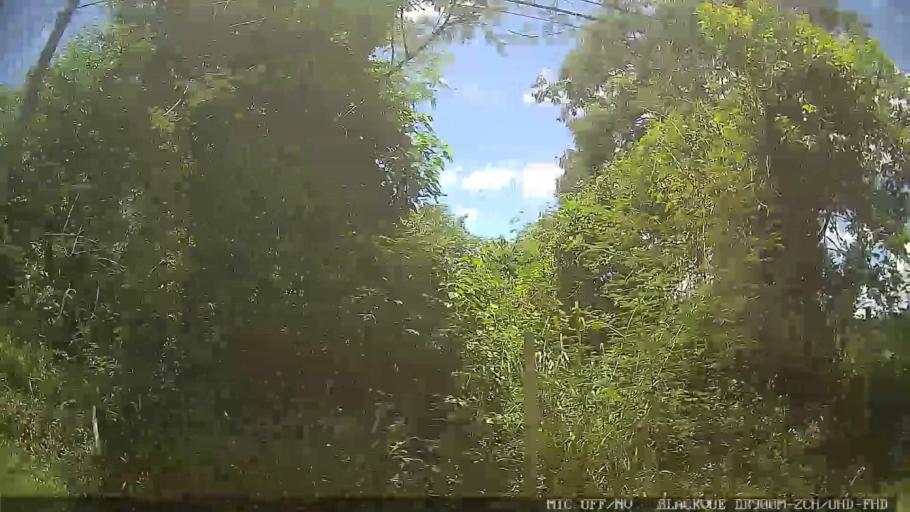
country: BR
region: Sao Paulo
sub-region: Atibaia
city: Atibaia
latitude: -23.0459
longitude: -46.5008
